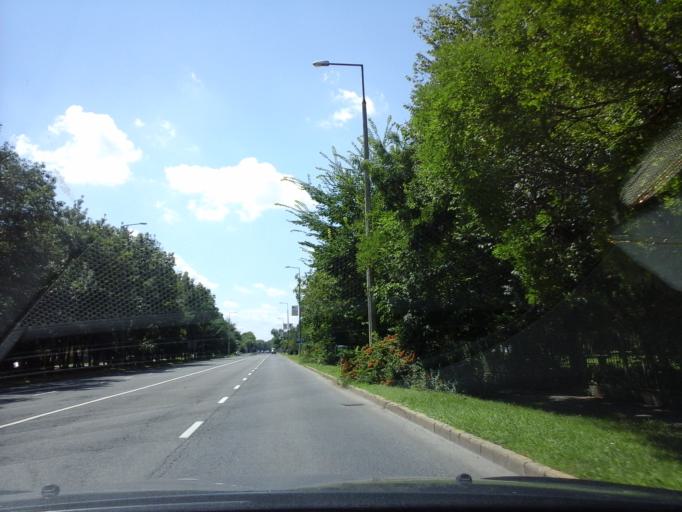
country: HU
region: Hajdu-Bihar
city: Hajduszoboszlo
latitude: 47.4510
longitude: 21.4083
